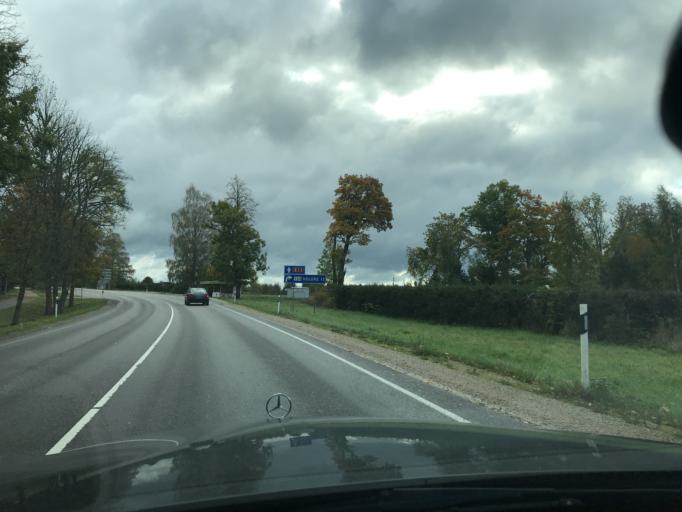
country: EE
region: Valgamaa
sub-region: Torva linn
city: Torva
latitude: 58.0147
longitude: 25.8805
